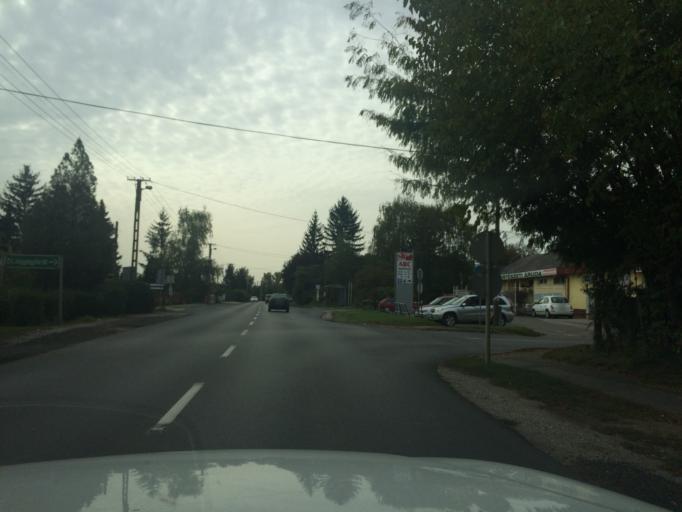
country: HU
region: Szabolcs-Szatmar-Bereg
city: Kotaj
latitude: 48.0088
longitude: 21.7373
